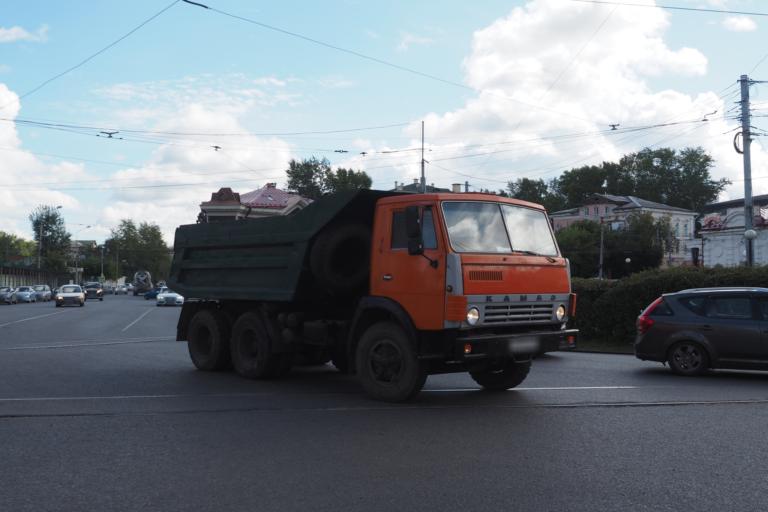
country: RU
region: Tomsk
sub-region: Tomskiy Rayon
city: Tomsk
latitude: 56.4845
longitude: 84.9515
